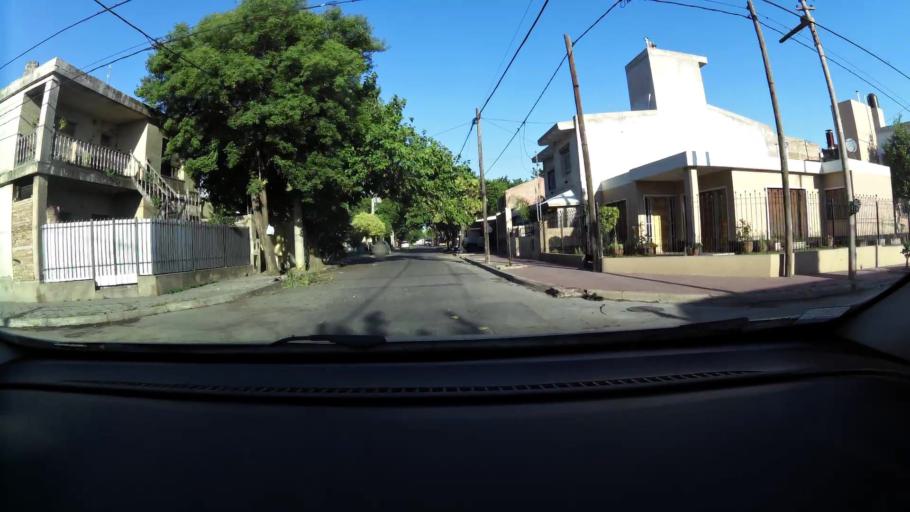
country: AR
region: Cordoba
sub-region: Departamento de Capital
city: Cordoba
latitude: -31.3771
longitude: -64.1929
